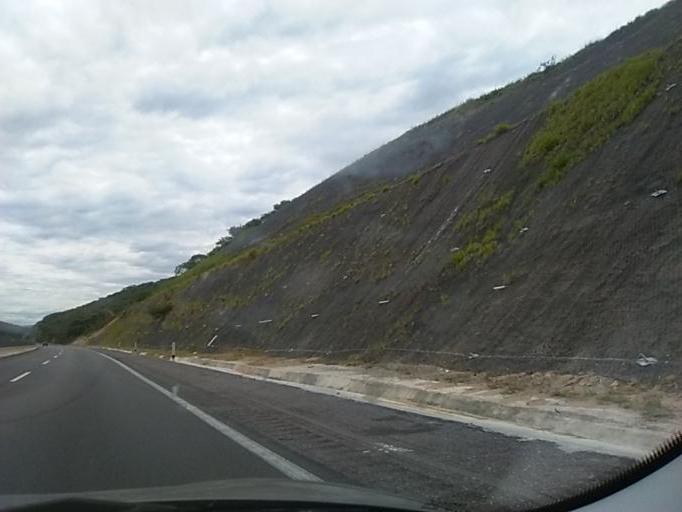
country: MX
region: Guerrero
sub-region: Huitzuco de los Figueroa
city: Ciudad de Huitzuco
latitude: 18.1465
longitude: -99.2120
